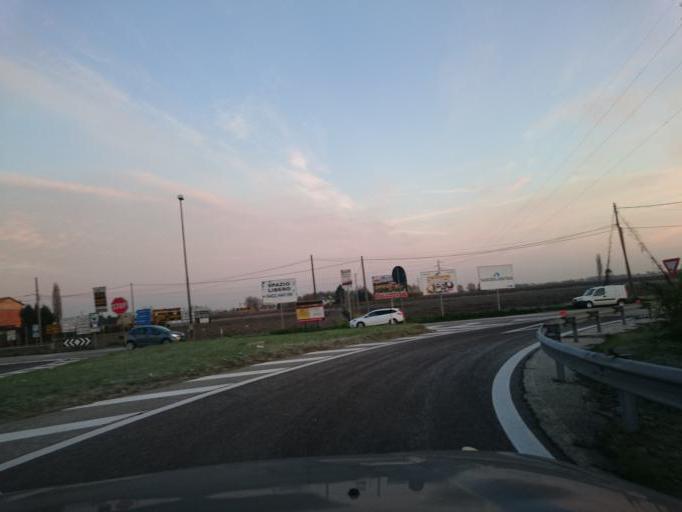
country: IT
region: Veneto
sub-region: Provincia di Padova
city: Carrara San Giorgio
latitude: 45.2947
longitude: 11.8017
